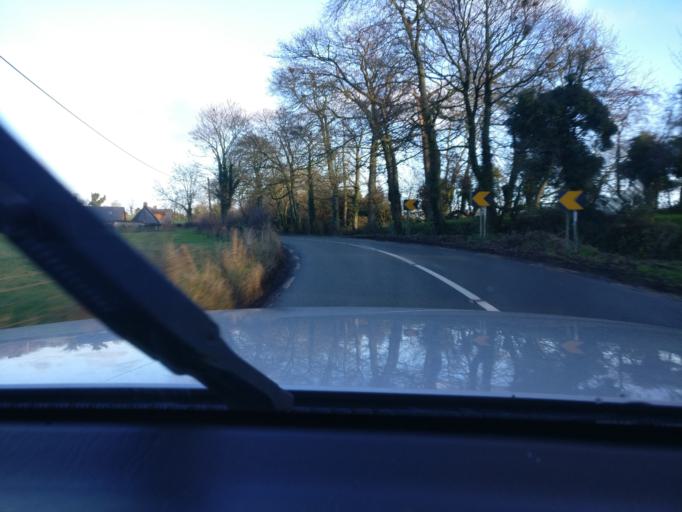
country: IE
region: Ulster
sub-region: An Cabhan
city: Kingscourt
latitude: 53.7970
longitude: -6.7100
